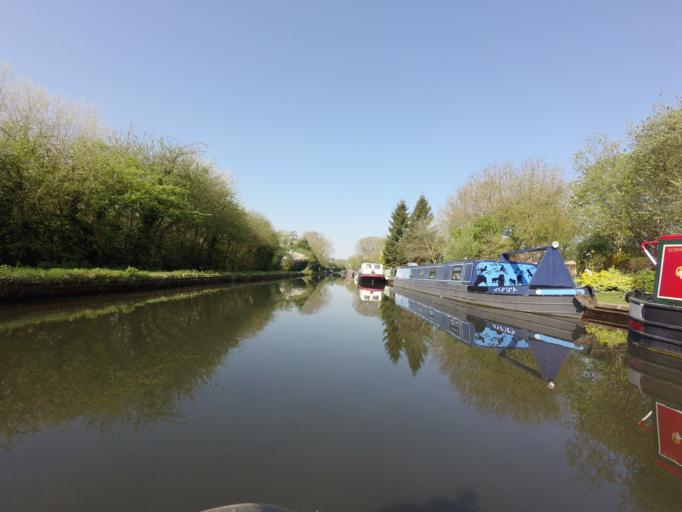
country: GB
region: England
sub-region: Hertfordshire
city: Bovingdon
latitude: 51.7470
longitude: -0.5195
